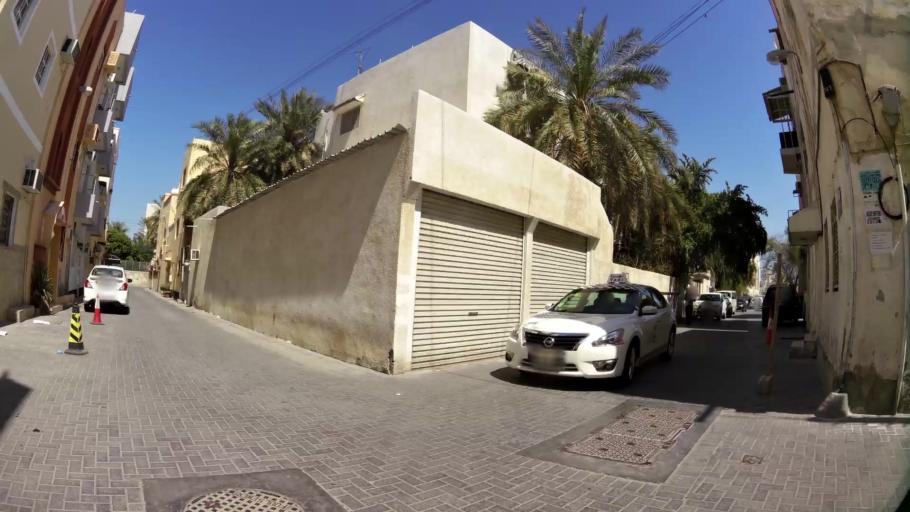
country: BH
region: Manama
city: Manama
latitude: 26.2227
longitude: 50.5903
